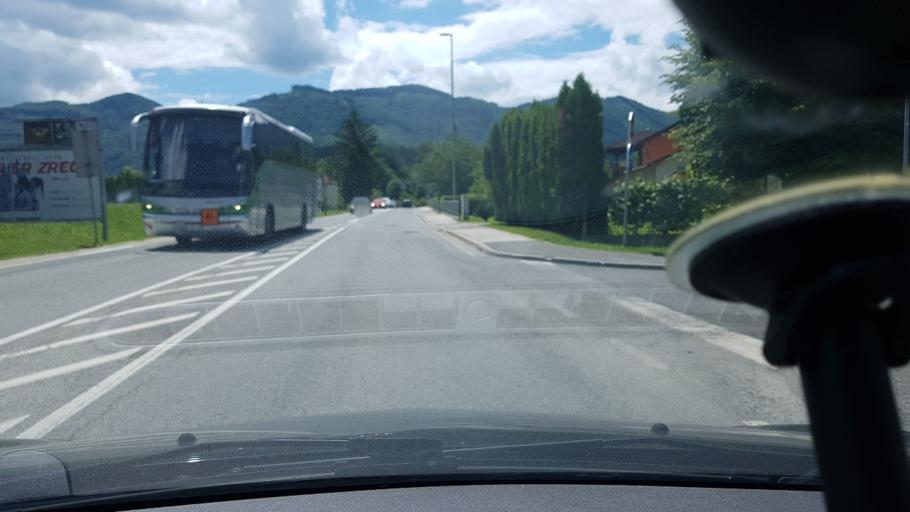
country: SI
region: Zrece
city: Zrece
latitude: 46.3661
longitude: 15.3937
